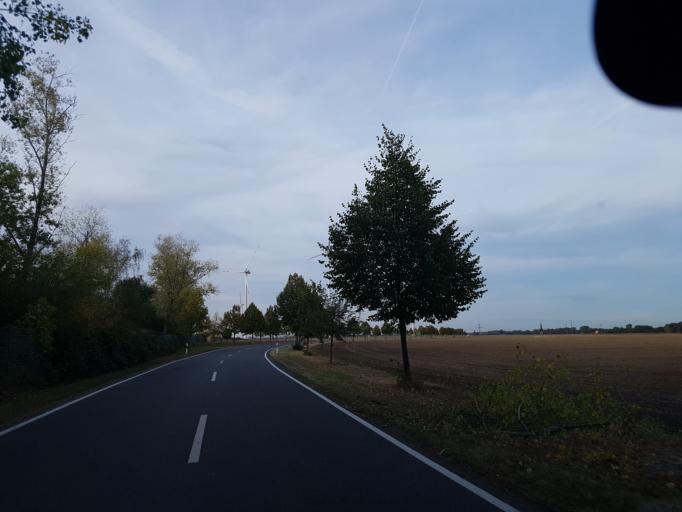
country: DE
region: Saxony
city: Glaubitz
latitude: 51.3318
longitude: 13.3749
